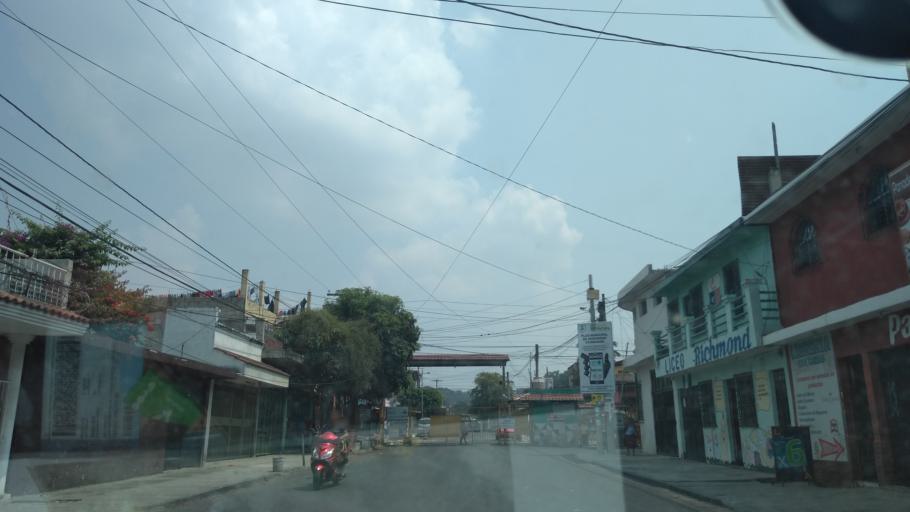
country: GT
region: Guatemala
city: Petapa
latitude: 14.5221
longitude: -90.5406
